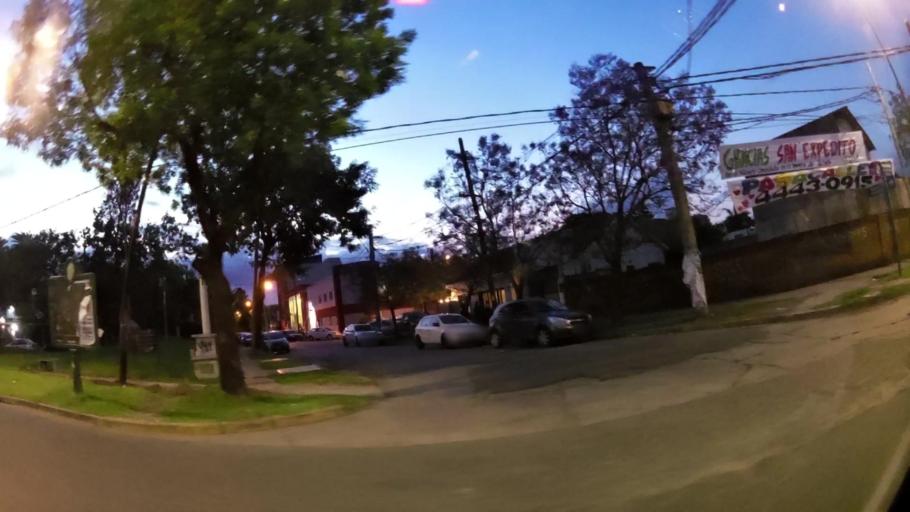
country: AR
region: Buenos Aires
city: Ituzaingo
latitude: -34.6544
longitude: -58.6595
